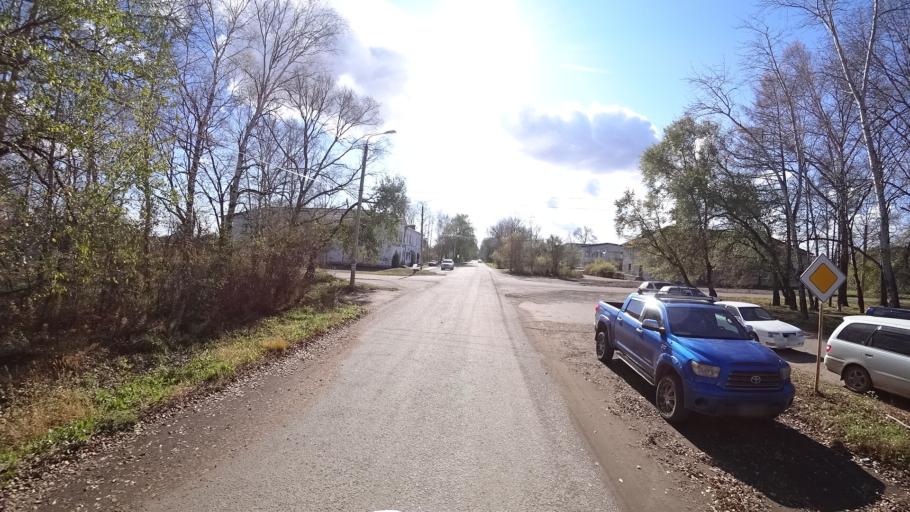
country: RU
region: Khabarovsk Krai
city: Amursk
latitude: 50.0997
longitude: 136.4972
